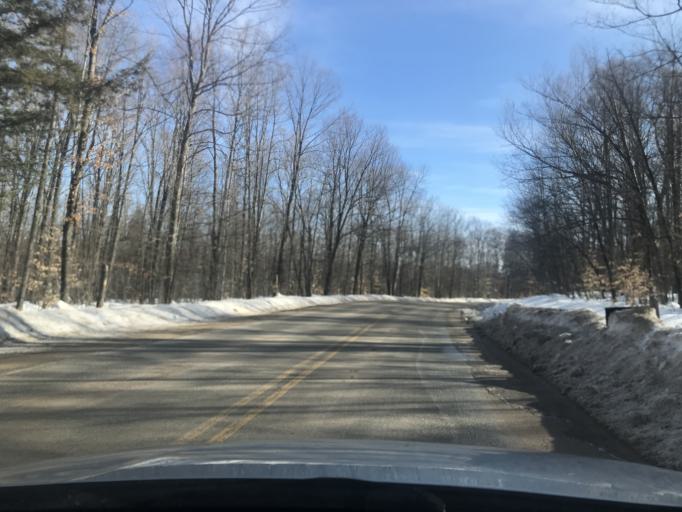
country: US
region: Michigan
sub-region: Dickinson County
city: Kingsford
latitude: 45.4183
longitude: -88.3988
